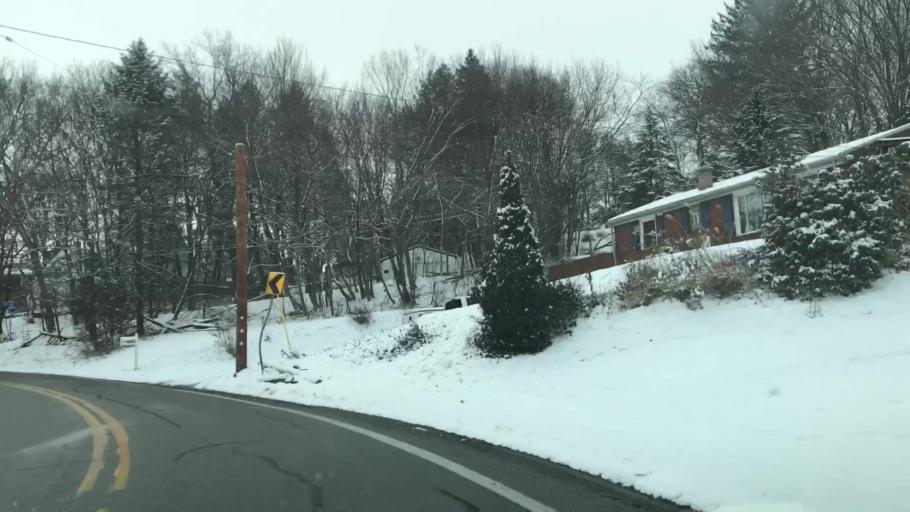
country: US
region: Pennsylvania
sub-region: Allegheny County
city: Allison Park
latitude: 40.5602
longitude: -79.9691
